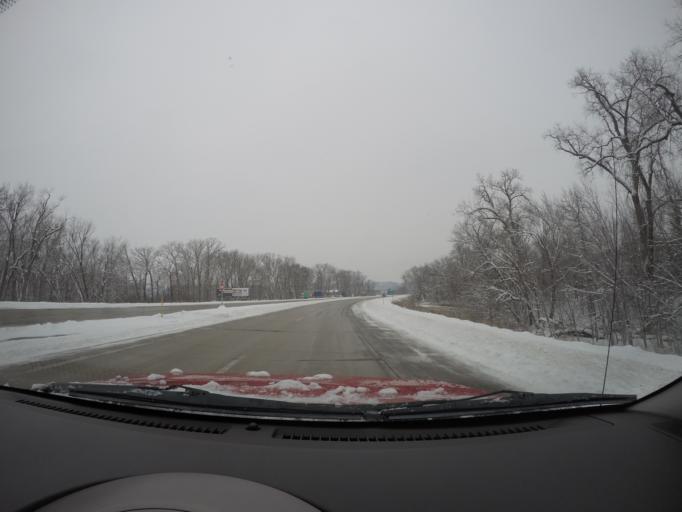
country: US
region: Minnesota
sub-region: Houston County
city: La Crescent
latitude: 43.8195
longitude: -91.2765
